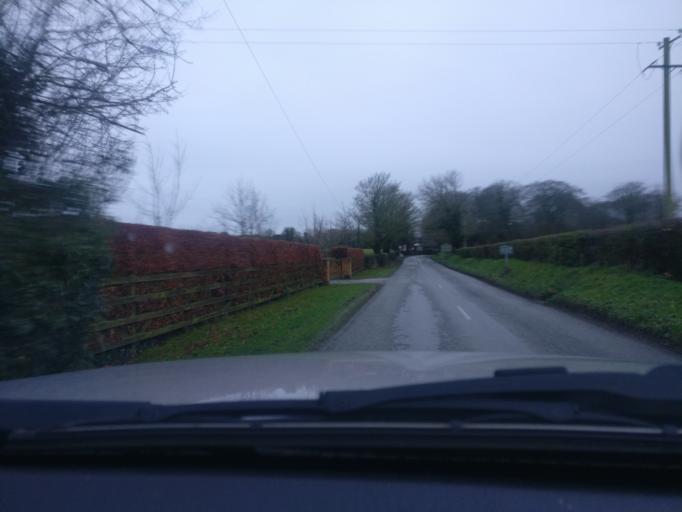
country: IE
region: Leinster
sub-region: Kildare
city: Kilcock
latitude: 53.4604
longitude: -6.6327
